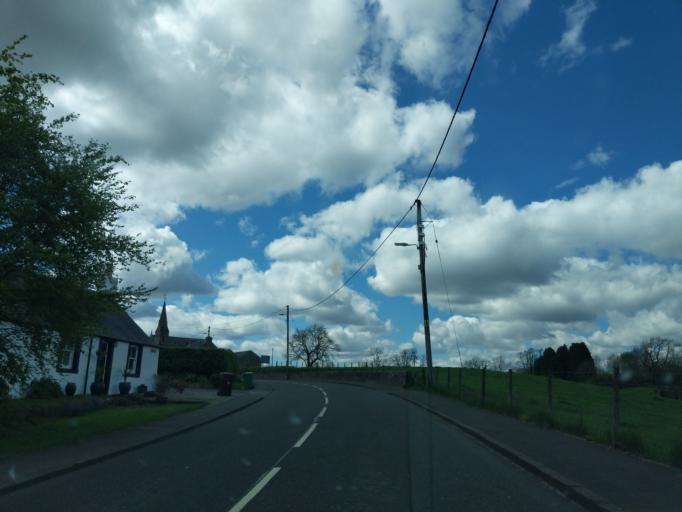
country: GB
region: Scotland
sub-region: Stirling
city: Doune
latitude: 56.1742
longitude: -4.1402
